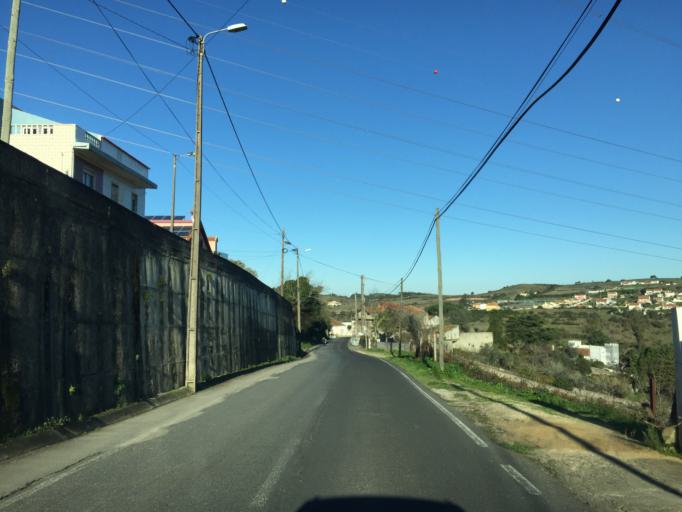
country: PT
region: Lisbon
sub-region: Odivelas
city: Canecas
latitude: 38.8228
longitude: -9.2351
